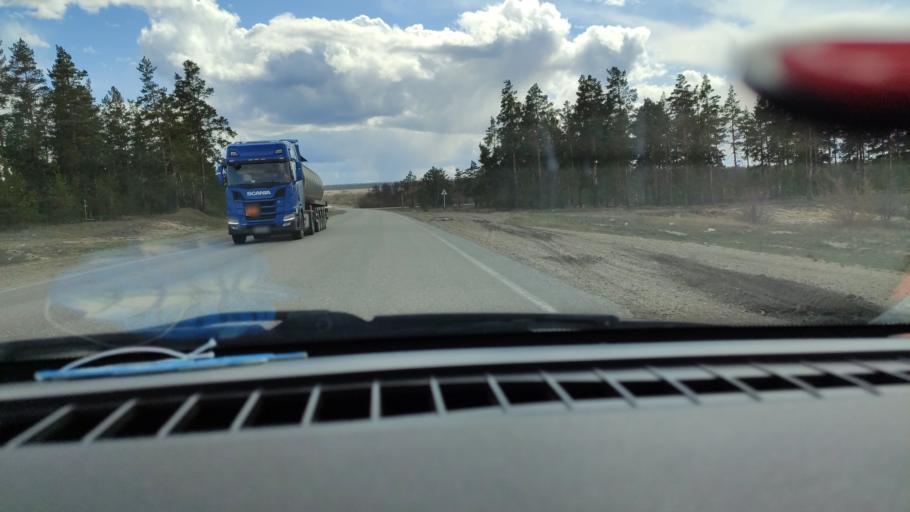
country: RU
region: Samara
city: Varlamovo
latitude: 53.1449
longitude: 48.2849
